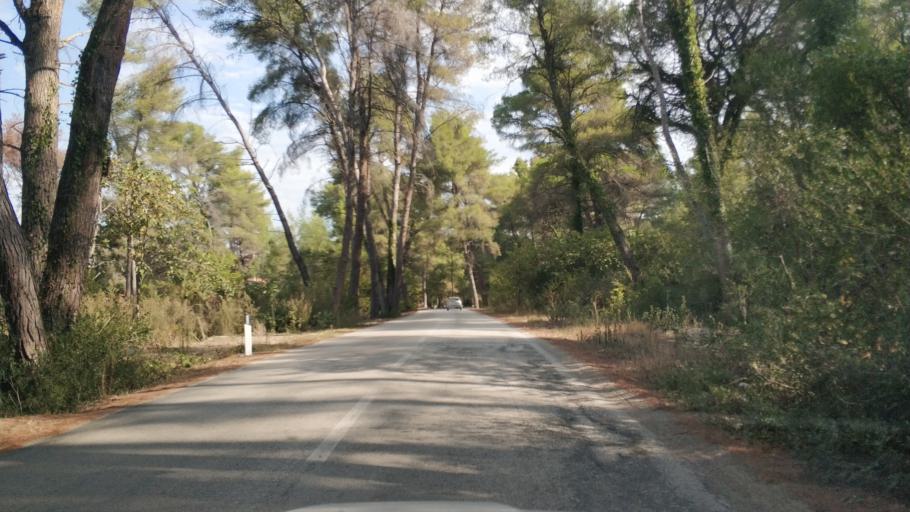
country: AL
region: Fier
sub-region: Rrethi i Lushnjes
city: Divjake
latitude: 40.9881
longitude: 19.4846
